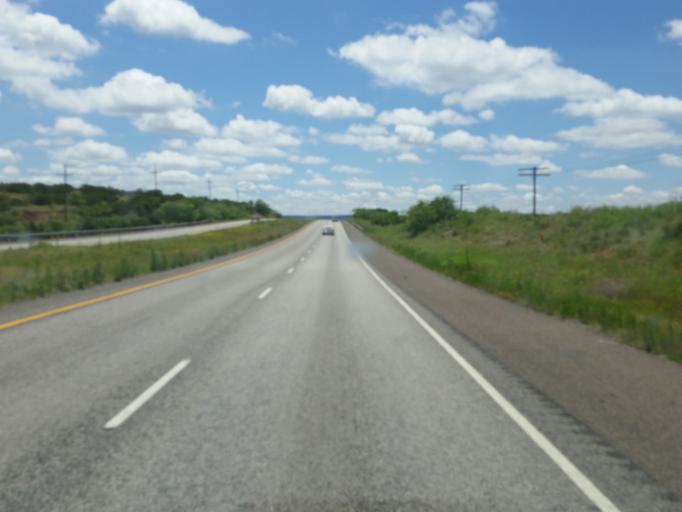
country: US
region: Texas
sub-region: Garza County
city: Post
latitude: 33.0243
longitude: -101.1834
